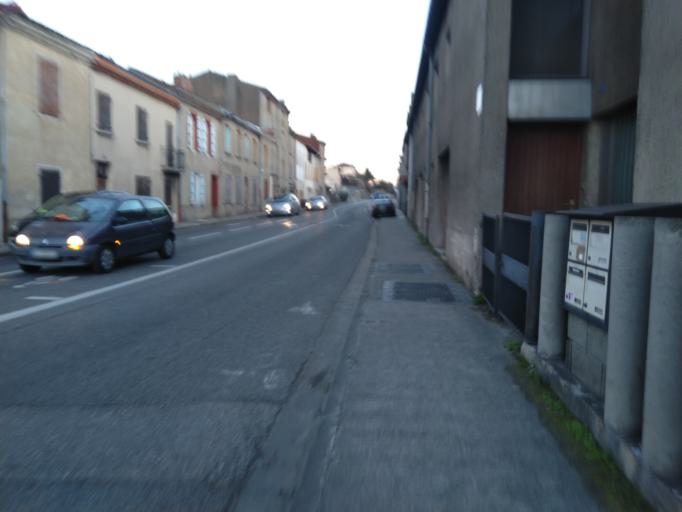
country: FR
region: Midi-Pyrenees
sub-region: Departement de l'Ariege
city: Pamiers
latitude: 43.1109
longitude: 1.6133
